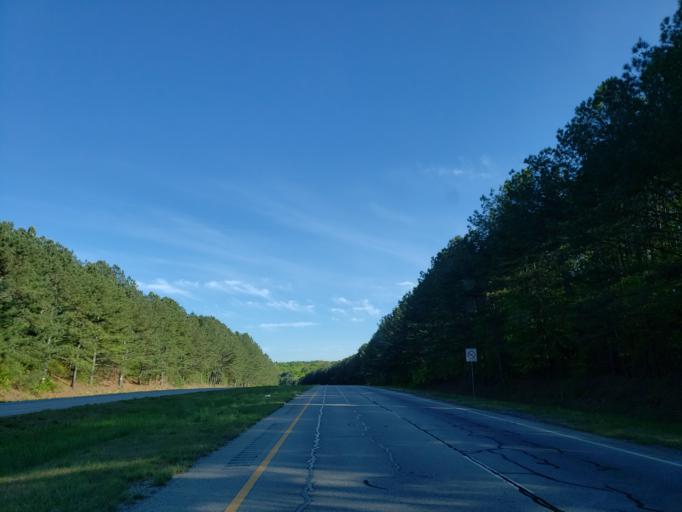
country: US
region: Georgia
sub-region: Polk County
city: Rockmart
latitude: 33.9463
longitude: -84.9800
